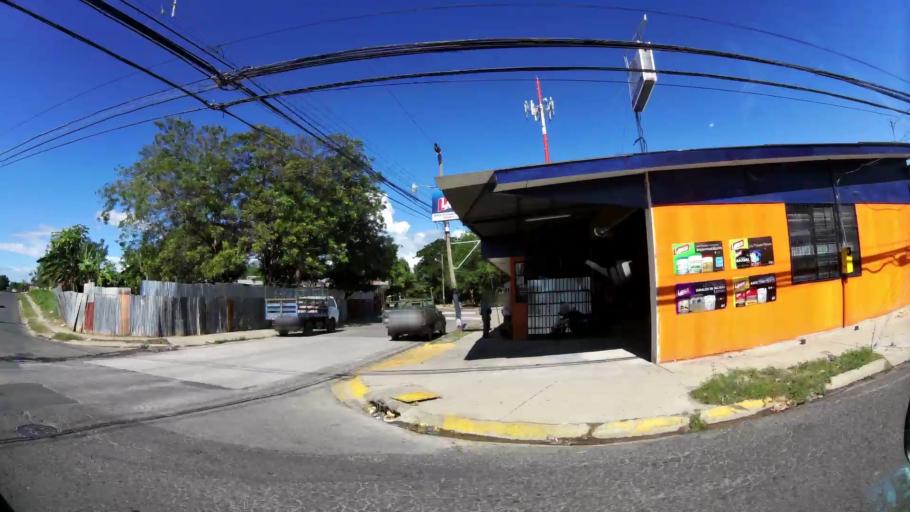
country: CR
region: Guanacaste
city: Liberia
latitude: 10.6374
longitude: -85.4363
